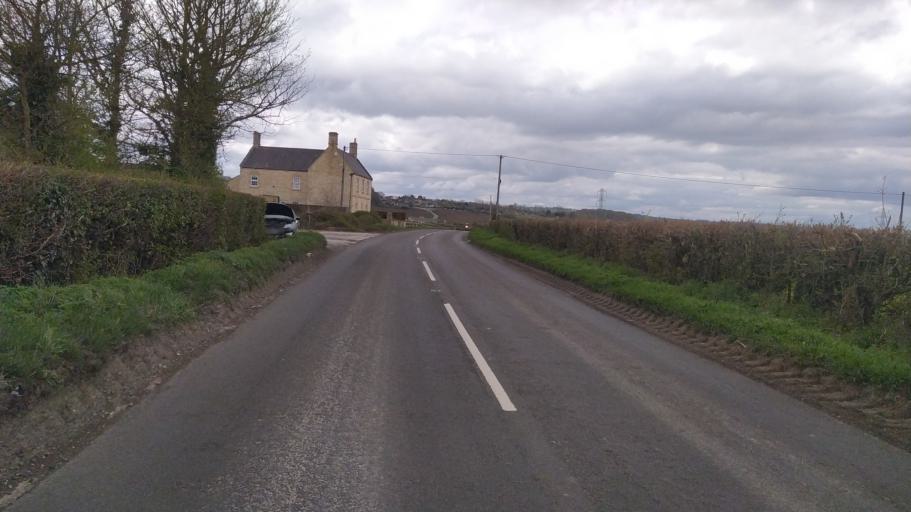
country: GB
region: England
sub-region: Wiltshire
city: Trowbridge
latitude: 51.3102
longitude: -2.1868
